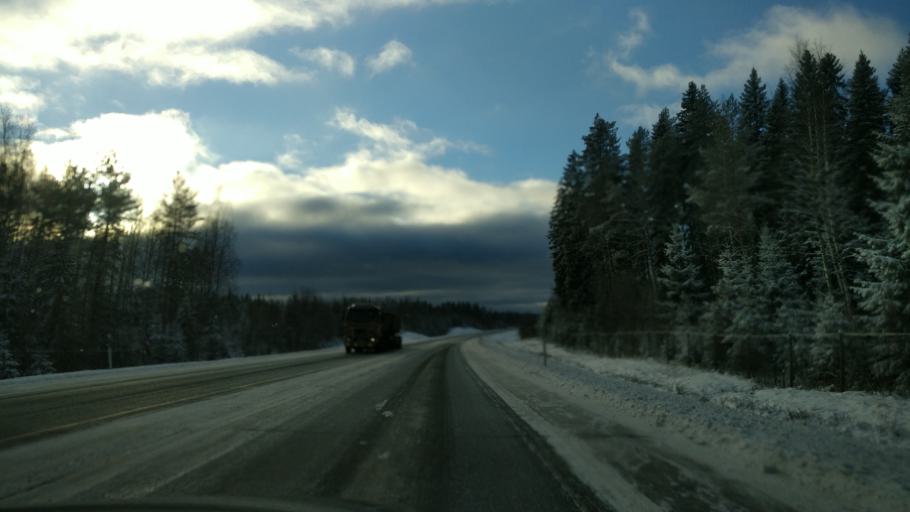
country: FI
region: Southern Savonia
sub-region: Mikkeli
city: Pertunmaa
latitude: 61.4079
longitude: 26.4066
